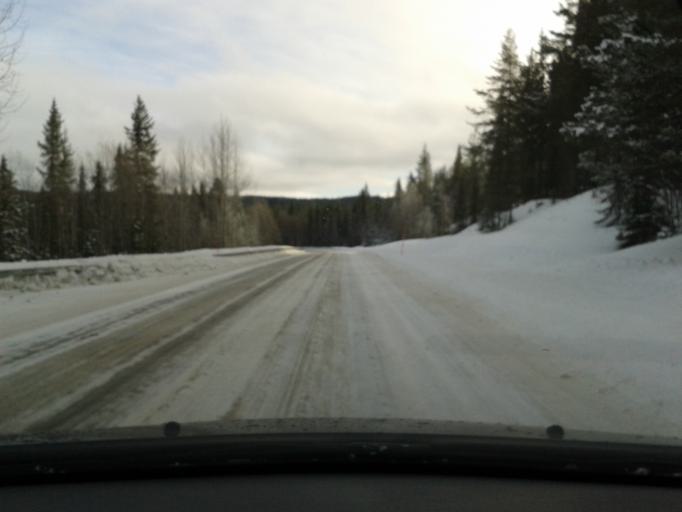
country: SE
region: Vaesterbotten
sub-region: Vilhelmina Kommun
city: Sjoberg
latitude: 64.7971
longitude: 16.0487
